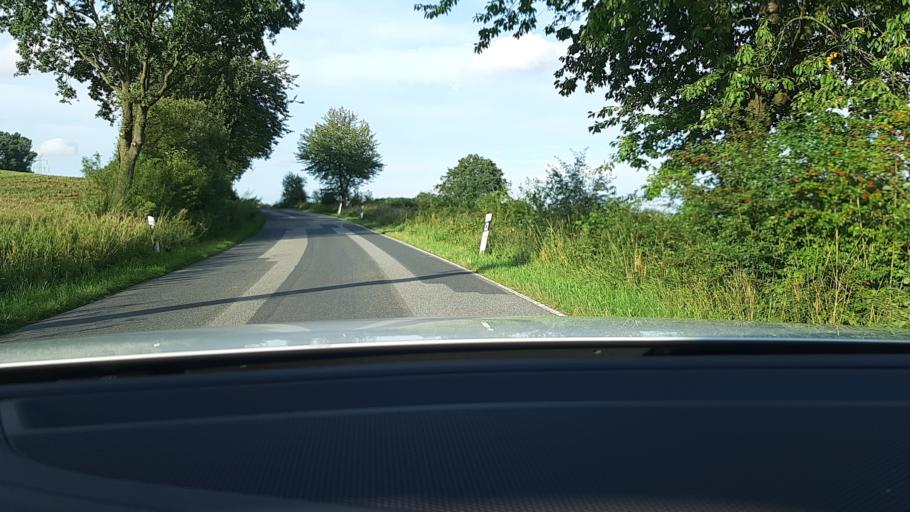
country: DE
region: Schleswig-Holstein
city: Monkhagen
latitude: 53.9057
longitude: 10.5504
